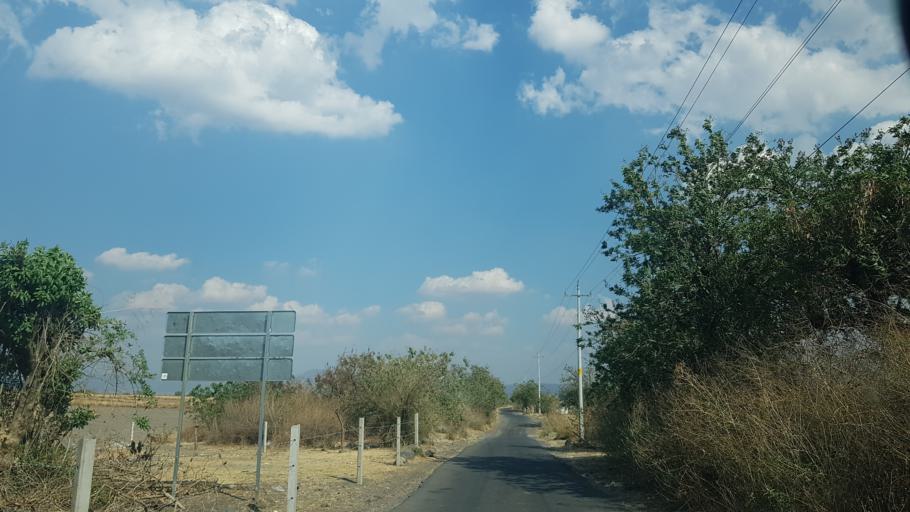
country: MX
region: Puebla
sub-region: Atlixco
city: Colonia Agricola de Ocotepec (Colonia San Jose)
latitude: 18.8927
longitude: -98.5085
